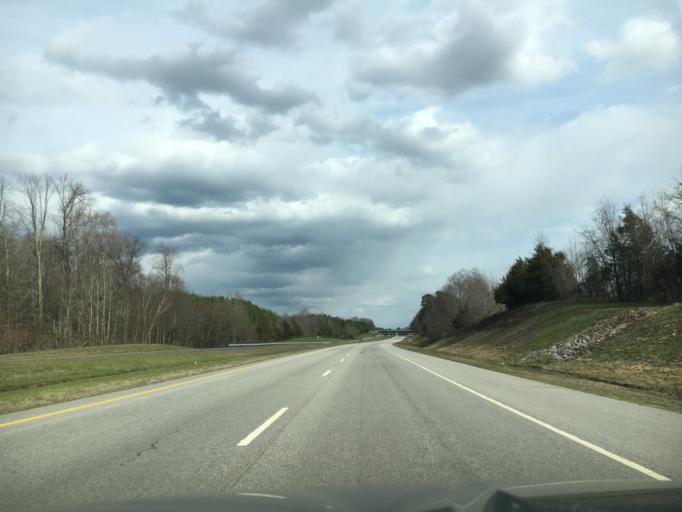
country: US
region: Virginia
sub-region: Mecklenburg County
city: South Hill
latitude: 36.7074
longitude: -78.1510
